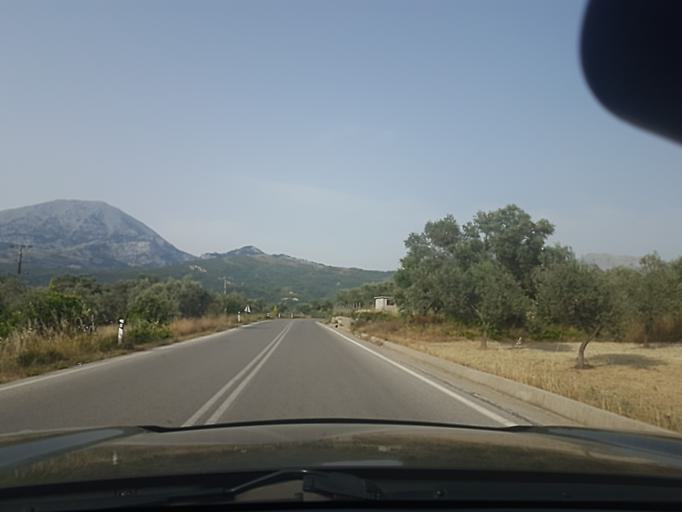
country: GR
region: Central Greece
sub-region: Nomos Evvoias
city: Yimnon
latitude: 38.5716
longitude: 23.7969
